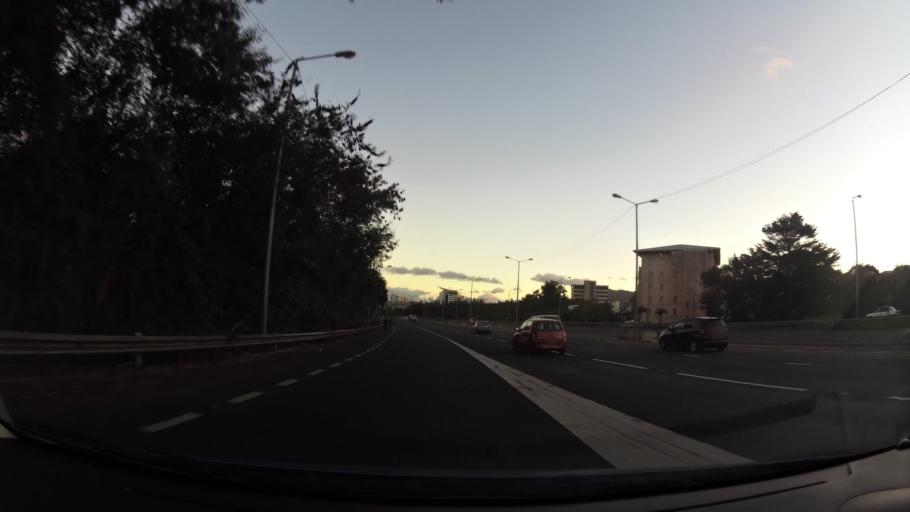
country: MU
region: Plaines Wilhems
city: Ebene
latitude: -20.2339
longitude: 57.5002
